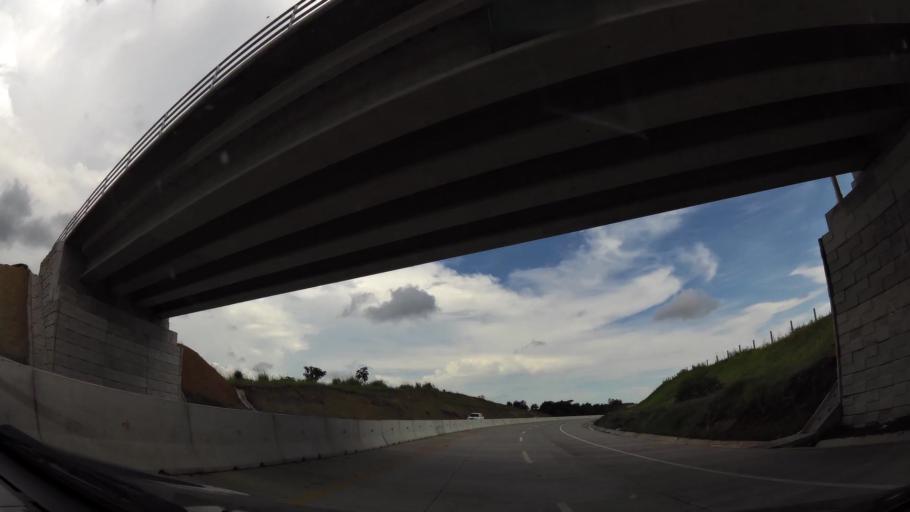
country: PA
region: Panama
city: Tocumen
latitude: 9.1044
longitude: -79.3953
